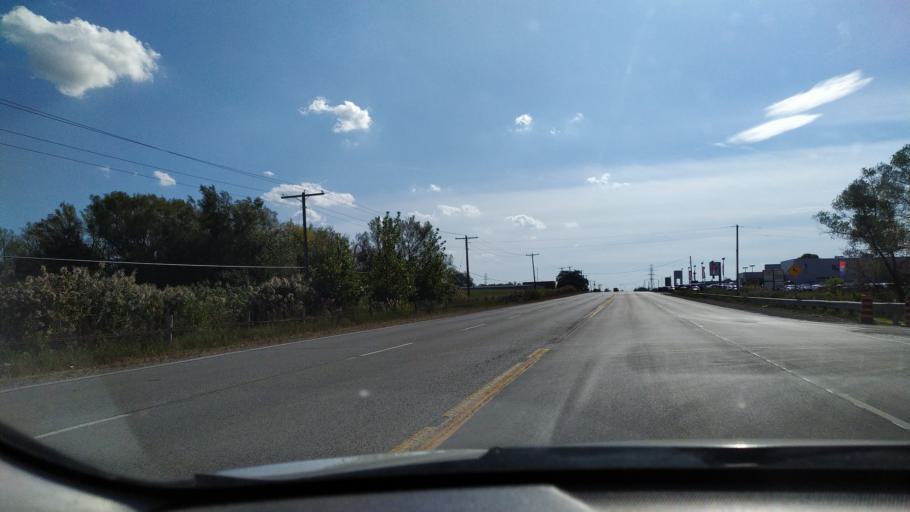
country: CA
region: Ontario
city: London
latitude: 42.9270
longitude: -81.2733
